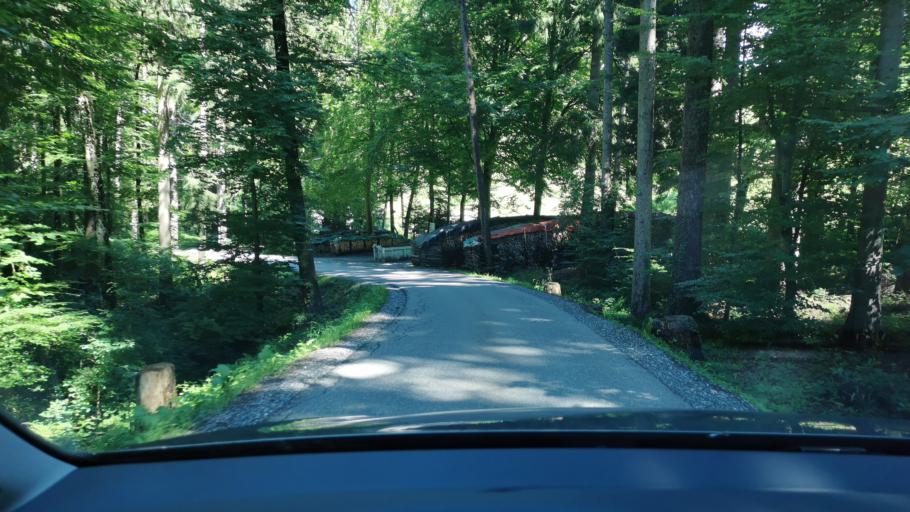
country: AT
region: Vorarlberg
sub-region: Politischer Bezirk Feldkirch
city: Viktorsberg
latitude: 47.2818
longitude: 9.6744
